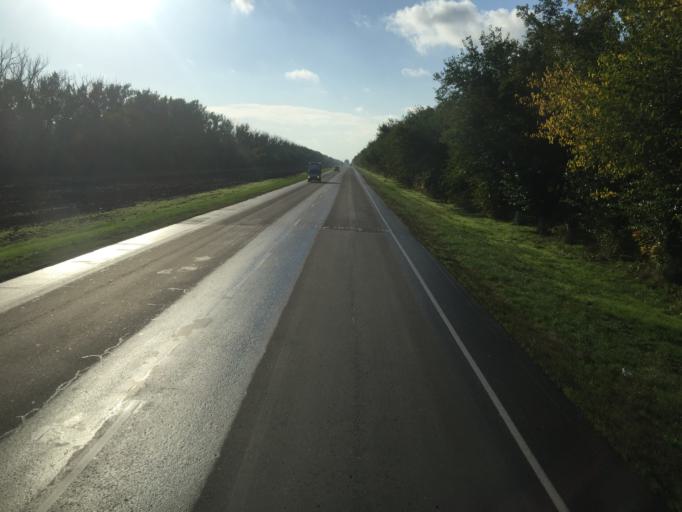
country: RU
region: Rostov
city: Yegorlykskaya
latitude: 46.6093
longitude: 40.6090
